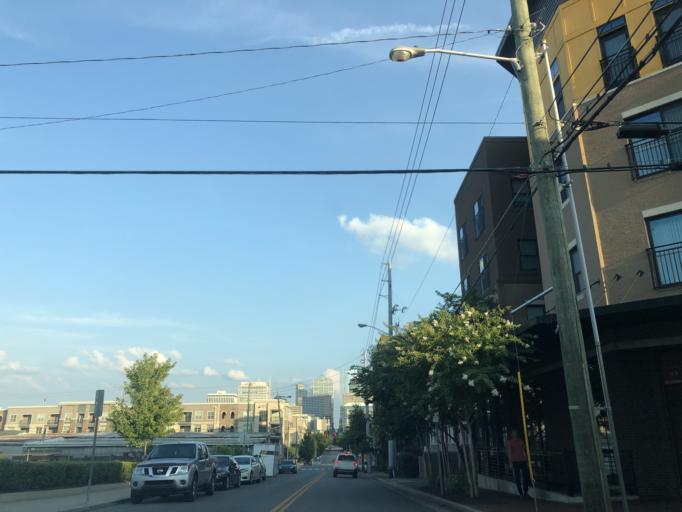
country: US
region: Tennessee
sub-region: Davidson County
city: Nashville
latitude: 36.1753
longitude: -86.7881
